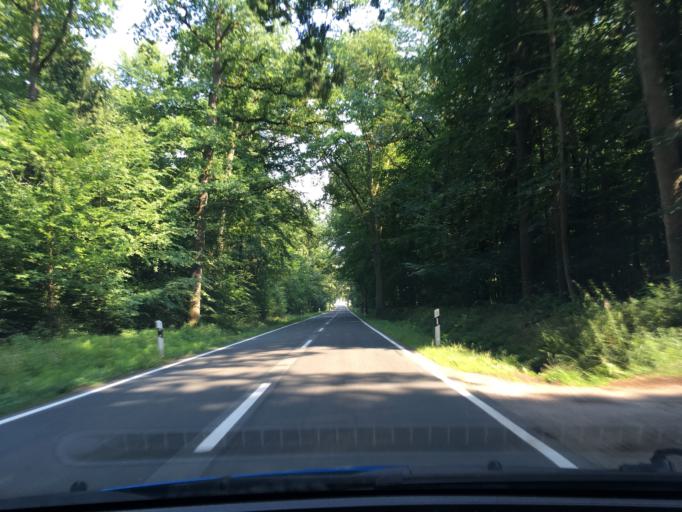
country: DE
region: Lower Saxony
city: Tosterglope
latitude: 53.2349
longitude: 10.8190
